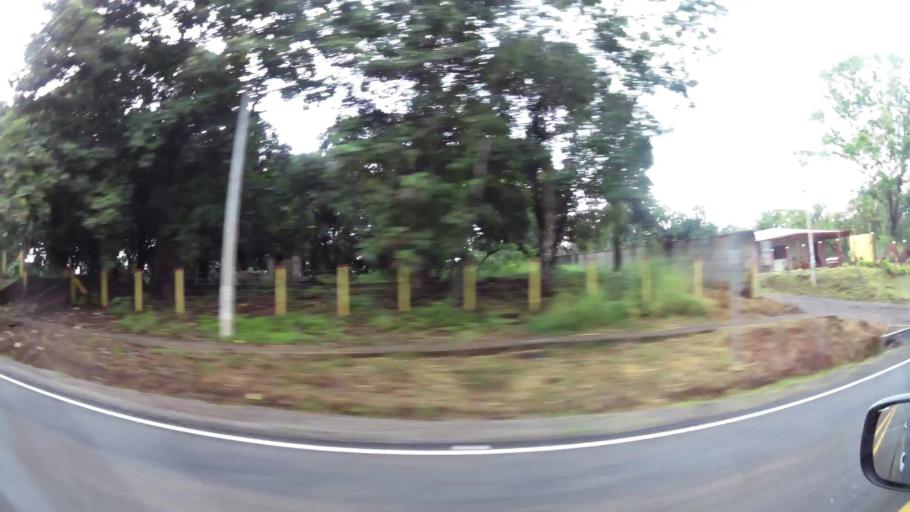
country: CR
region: Alajuela
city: Orotina
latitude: 9.9458
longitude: -84.5524
